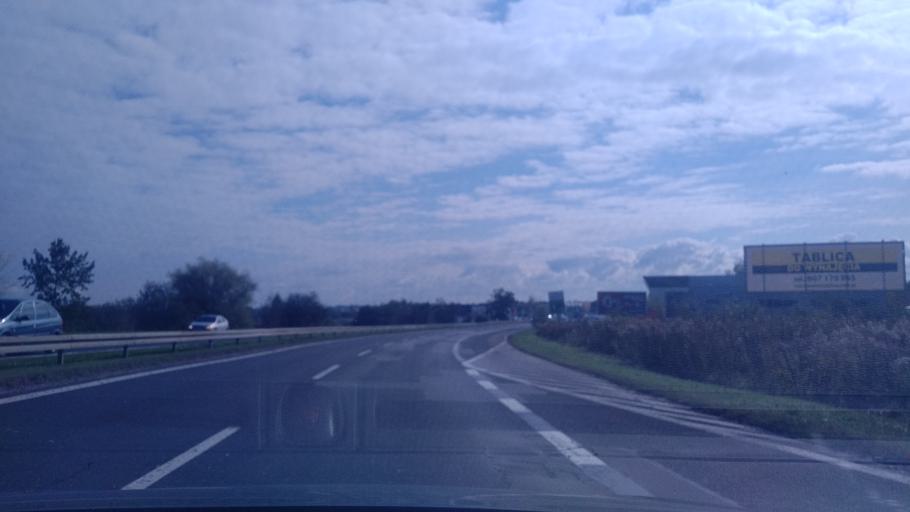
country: PL
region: Lesser Poland Voivodeship
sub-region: Powiat krakowski
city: Modlnica
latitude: 50.1036
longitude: 19.8866
